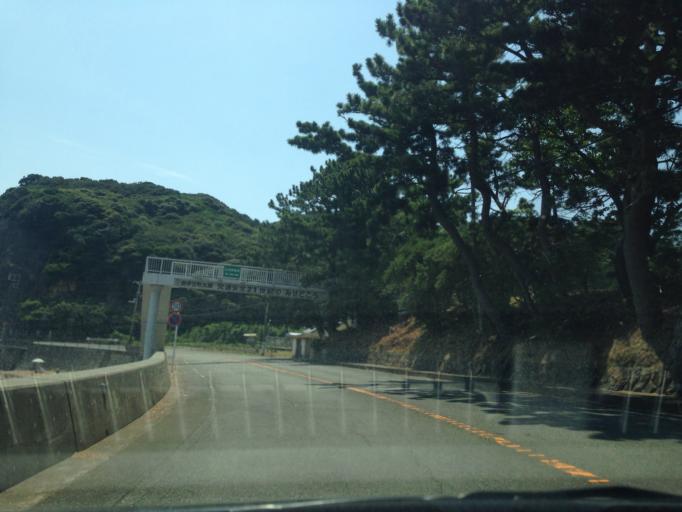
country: JP
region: Shizuoka
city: Shimoda
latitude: 34.6200
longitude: 138.8655
